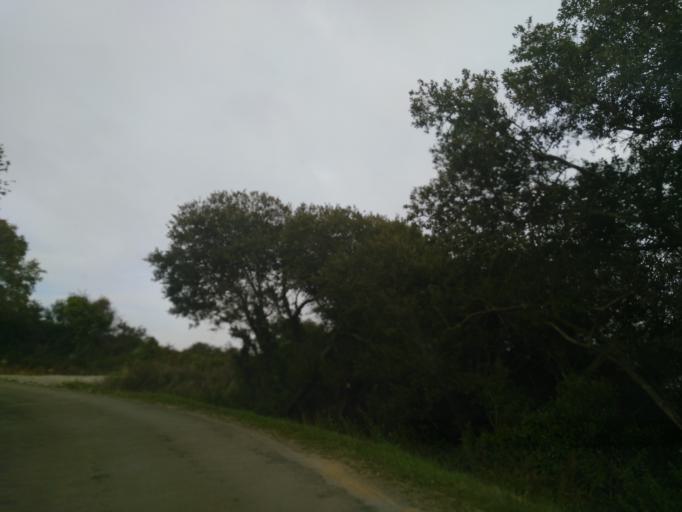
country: FR
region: Brittany
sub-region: Departement du Finistere
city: Crozon
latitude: 48.2384
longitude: -4.4424
